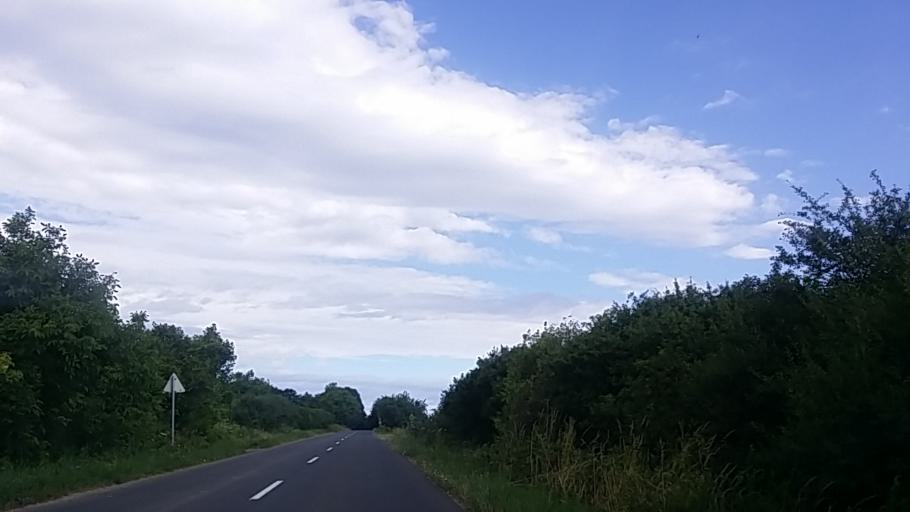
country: HU
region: Nograd
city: Romhany
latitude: 47.8599
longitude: 19.2645
